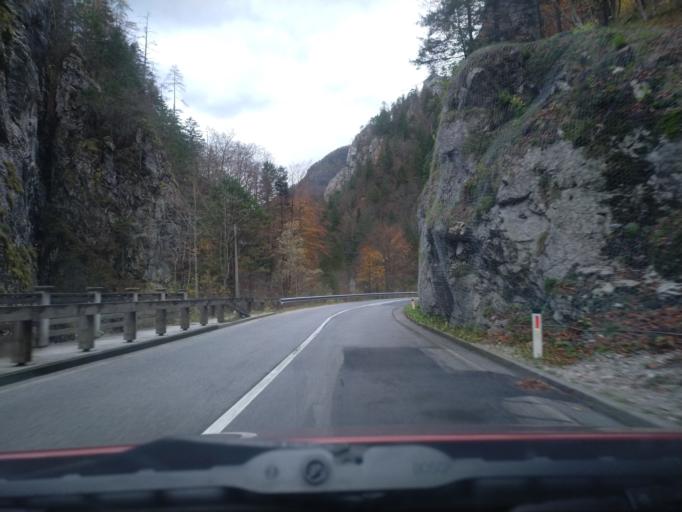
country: SI
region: Luce
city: Luce
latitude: 46.3804
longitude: 14.7273
